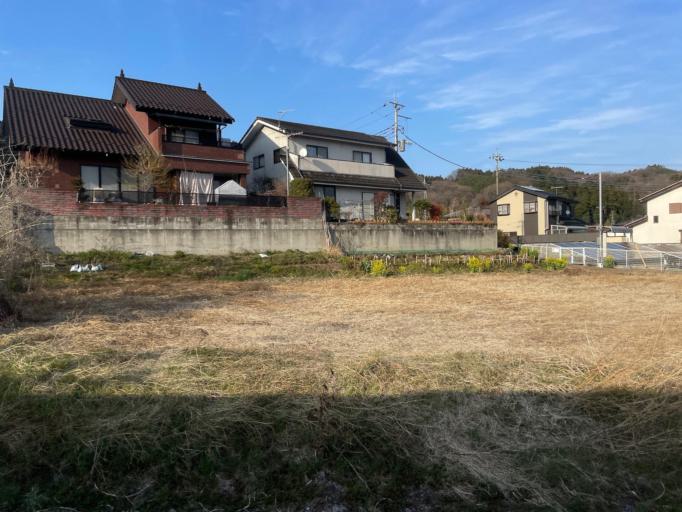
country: JP
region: Gunma
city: Annaka
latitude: 36.3182
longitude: 138.7834
